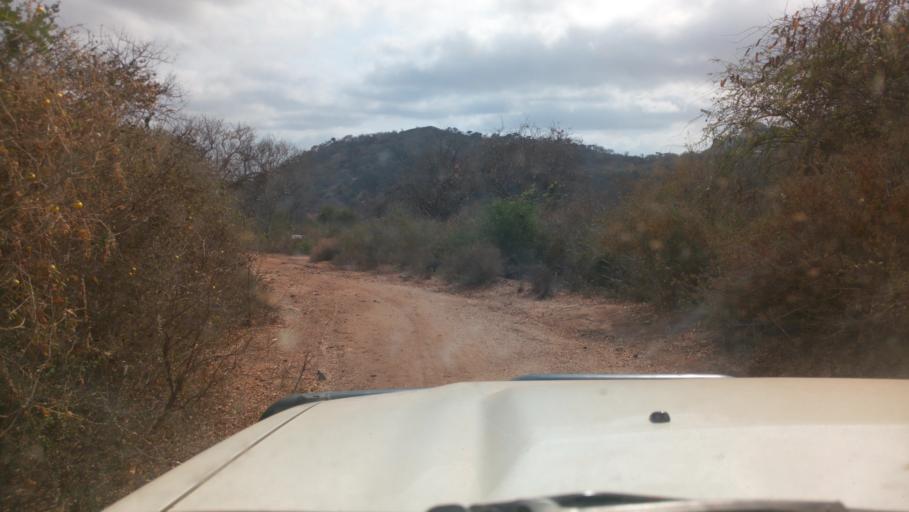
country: KE
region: Kitui
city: Kitui
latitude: -1.8556
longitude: 38.2936
